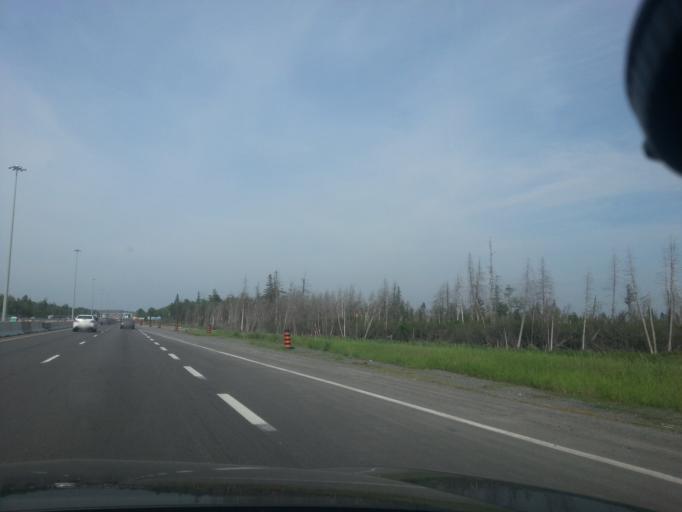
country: CA
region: Ontario
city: Bells Corners
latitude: 45.2824
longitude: -75.9545
